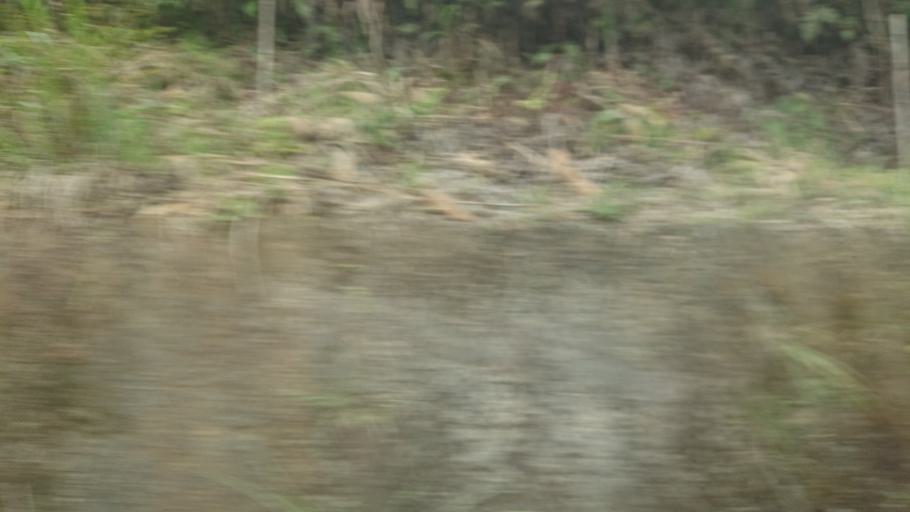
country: TW
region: Taiwan
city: Lugu
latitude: 23.6266
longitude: 120.7098
